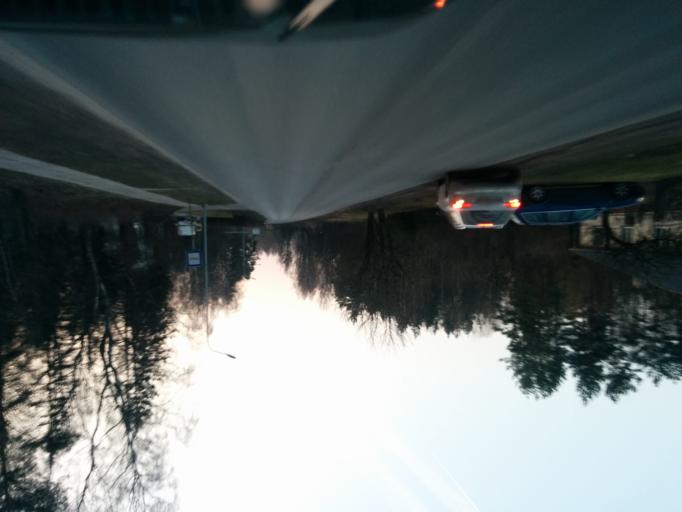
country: LV
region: Kekava
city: Balozi
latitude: 56.8715
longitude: 24.1121
